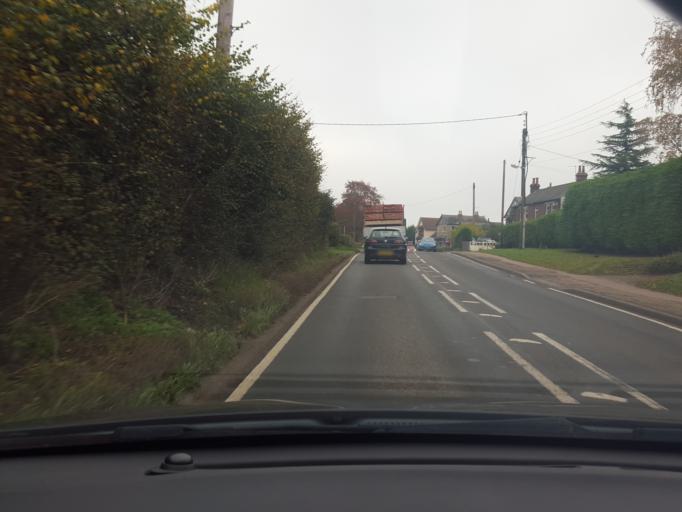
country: GB
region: England
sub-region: Essex
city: Brightlingsea
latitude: 51.8339
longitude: 1.0229
